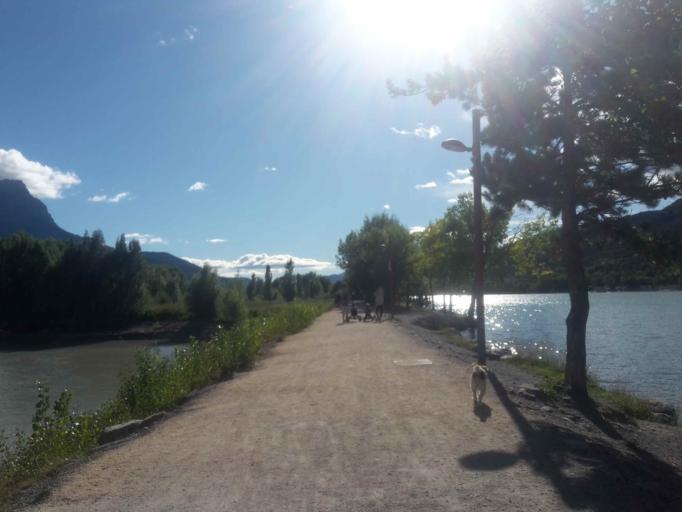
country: FR
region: Provence-Alpes-Cote d'Azur
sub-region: Departement des Hautes-Alpes
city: Embrun
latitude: 44.5480
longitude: 6.4754
